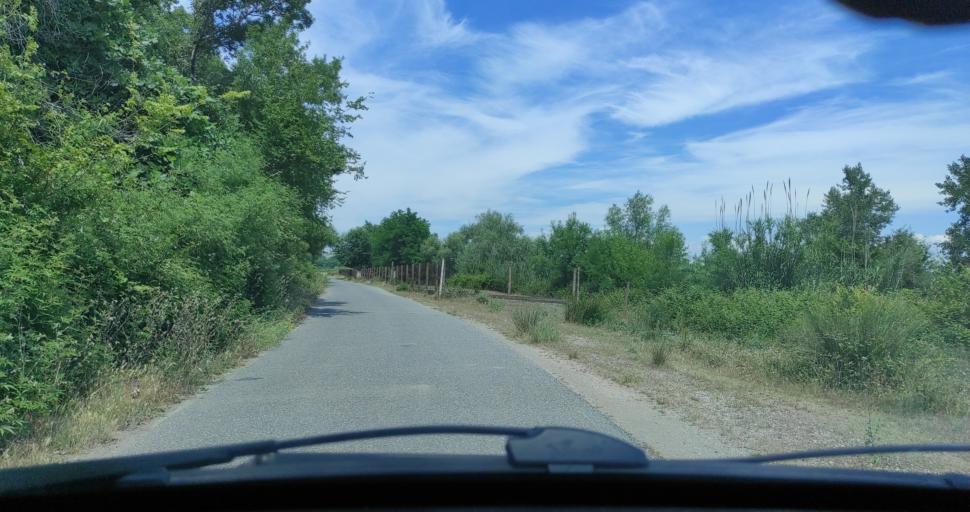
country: AL
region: Shkoder
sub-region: Rrethi i Shkodres
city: Velipoje
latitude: 41.8768
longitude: 19.3839
